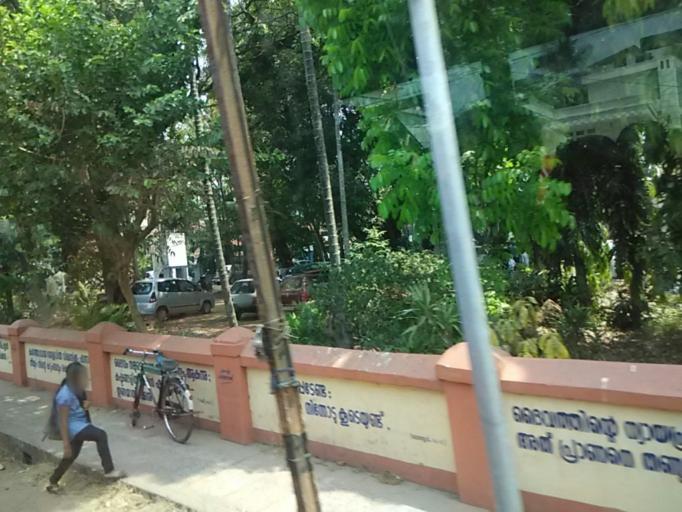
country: IN
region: Kerala
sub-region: Kozhikode
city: Kozhikode
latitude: 11.2683
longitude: 75.7767
